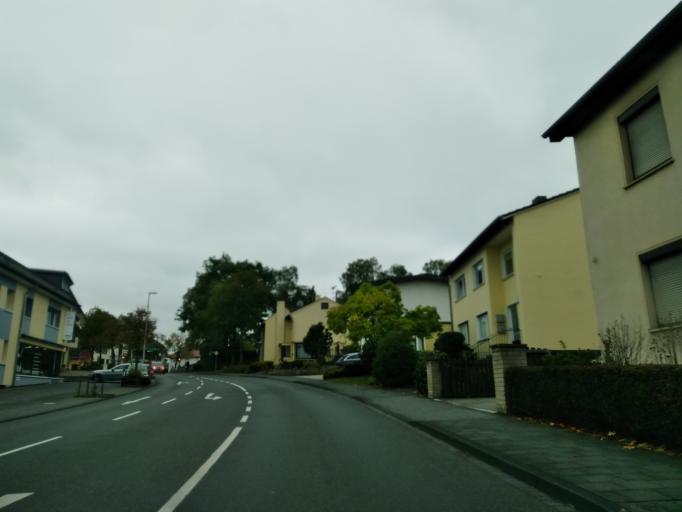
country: DE
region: Rheinland-Pfalz
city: Windhagen
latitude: 50.6633
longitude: 7.3010
